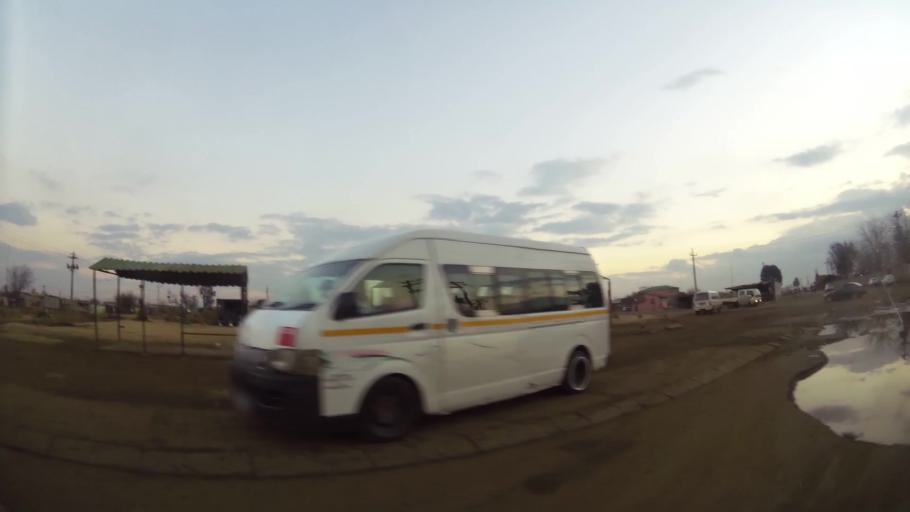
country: ZA
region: Gauteng
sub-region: City of Johannesburg Metropolitan Municipality
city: Orange Farm
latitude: -26.5460
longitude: 27.8428
